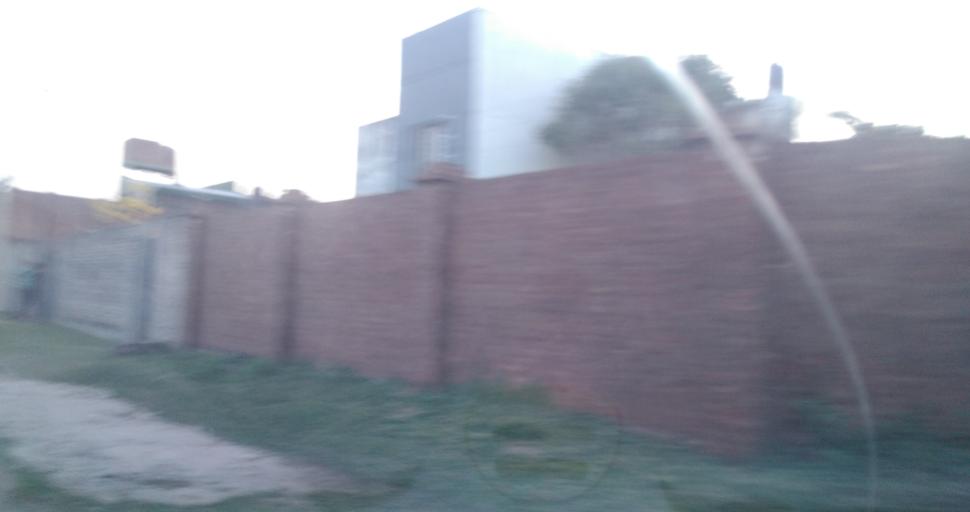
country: AR
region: Chaco
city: Fontana
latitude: -27.4319
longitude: -59.0020
